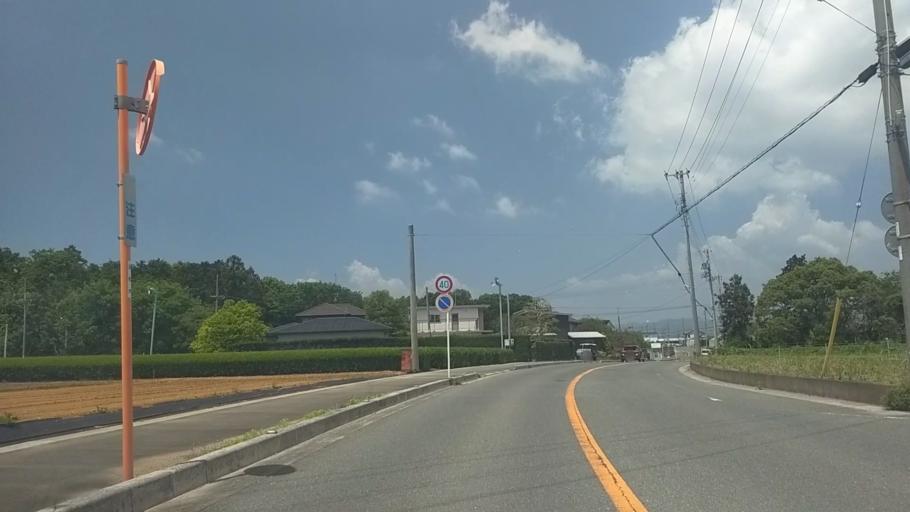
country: JP
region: Shizuoka
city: Hamamatsu
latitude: 34.7541
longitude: 137.6815
